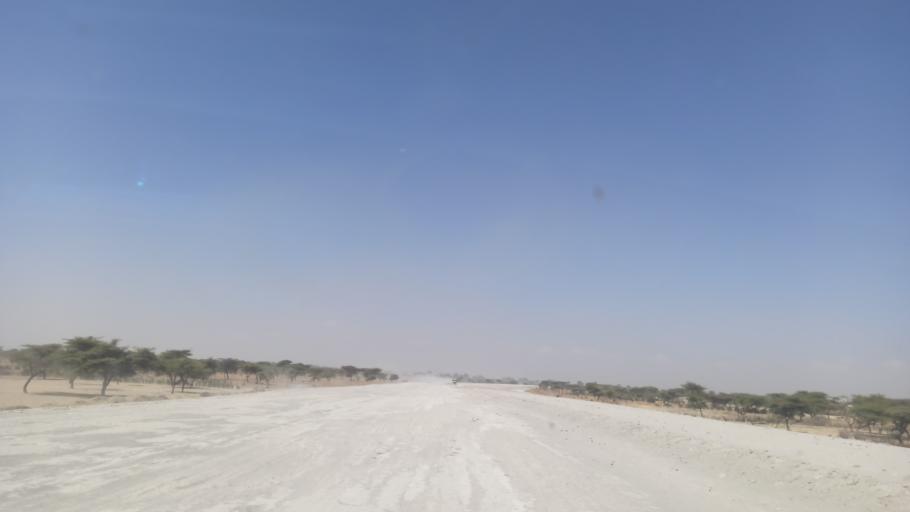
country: ET
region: Oromiya
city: Ziway
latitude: 7.6925
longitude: 38.6542
